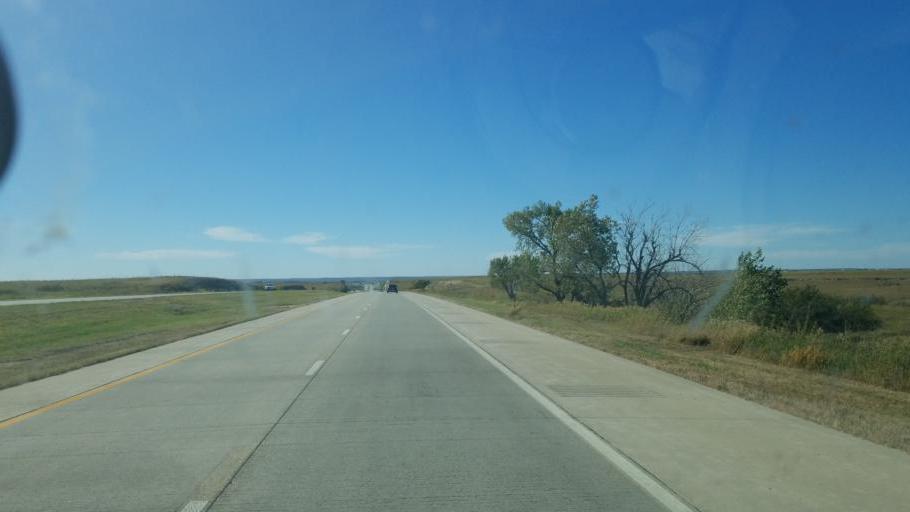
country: US
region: Kansas
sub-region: Riley County
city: Ogden
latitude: 39.0653
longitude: -96.6893
